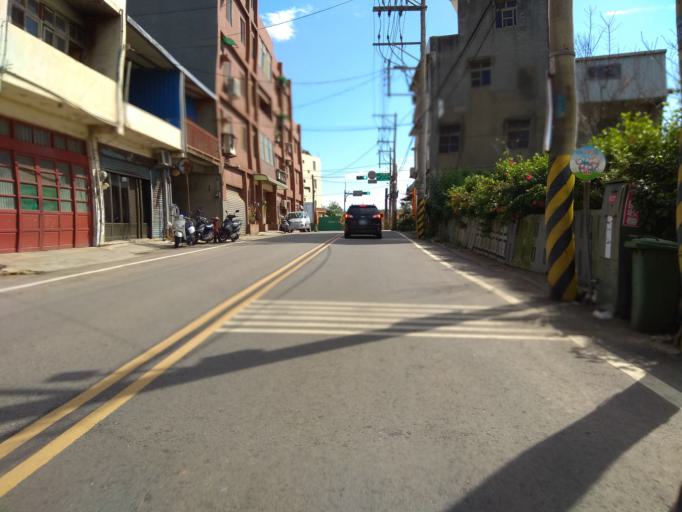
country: TW
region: Taiwan
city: Taoyuan City
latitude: 25.0387
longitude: 121.1289
